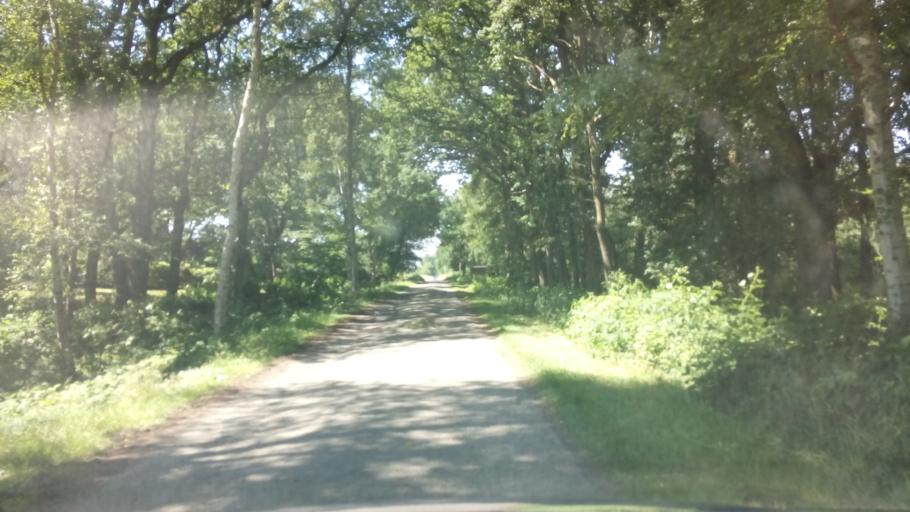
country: DE
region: Lower Saxony
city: Hambergen
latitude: 53.2682
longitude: 8.8485
